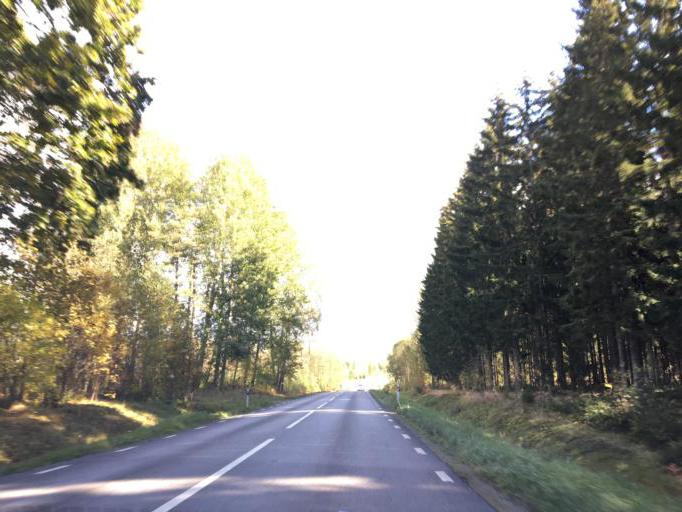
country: SE
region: Soedermanland
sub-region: Nykopings Kommun
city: Olstorp
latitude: 58.9077
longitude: 16.5577
